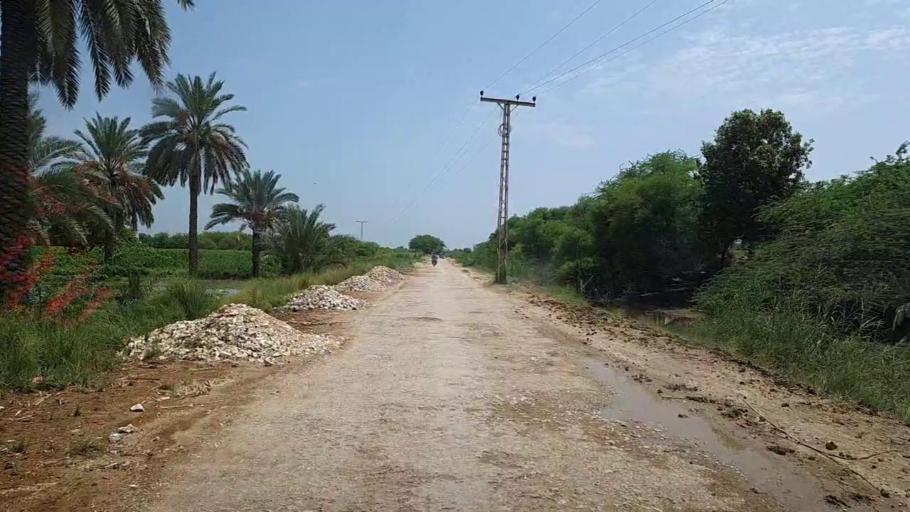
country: PK
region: Sindh
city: Bhiria
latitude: 26.9003
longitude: 68.1986
